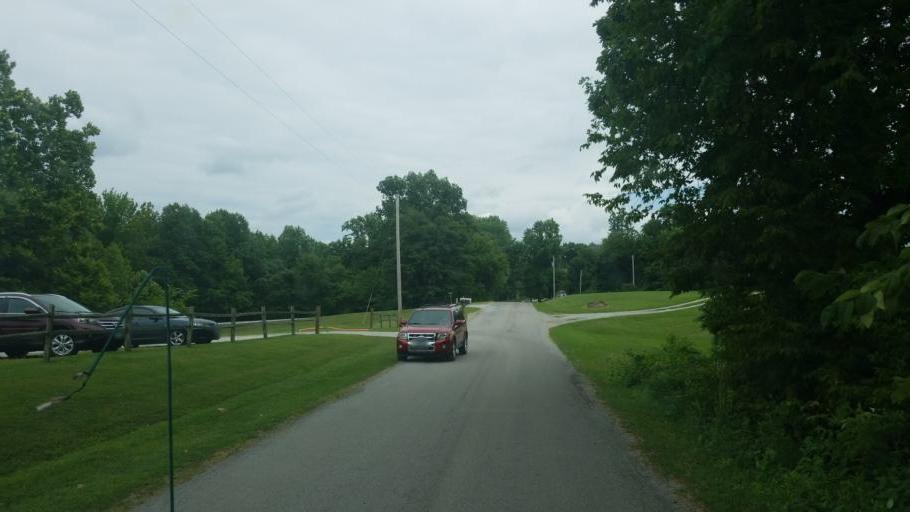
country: US
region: Illinois
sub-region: Jackson County
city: Murphysboro
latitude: 37.6718
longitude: -89.3865
